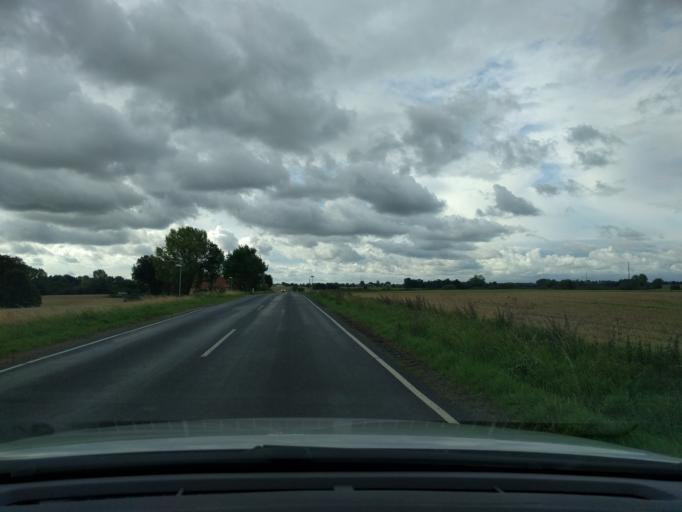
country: DK
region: South Denmark
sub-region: Nyborg Kommune
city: Ullerslev
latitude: 55.3761
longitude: 10.6667
